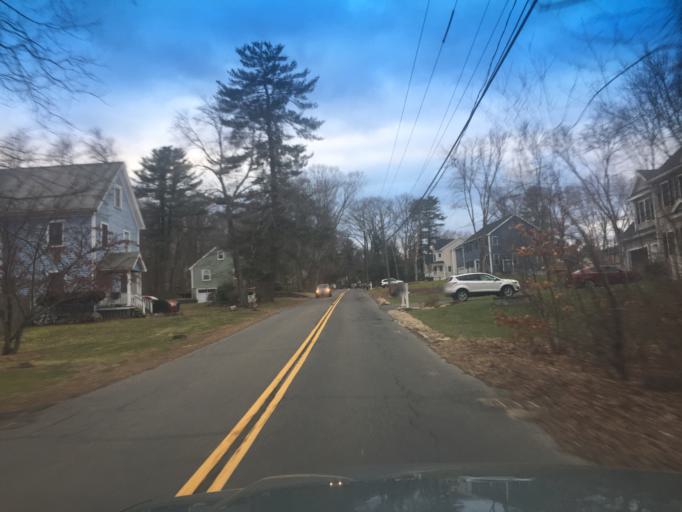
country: US
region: Massachusetts
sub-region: Norfolk County
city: Millis
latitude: 42.1592
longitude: -71.3720
